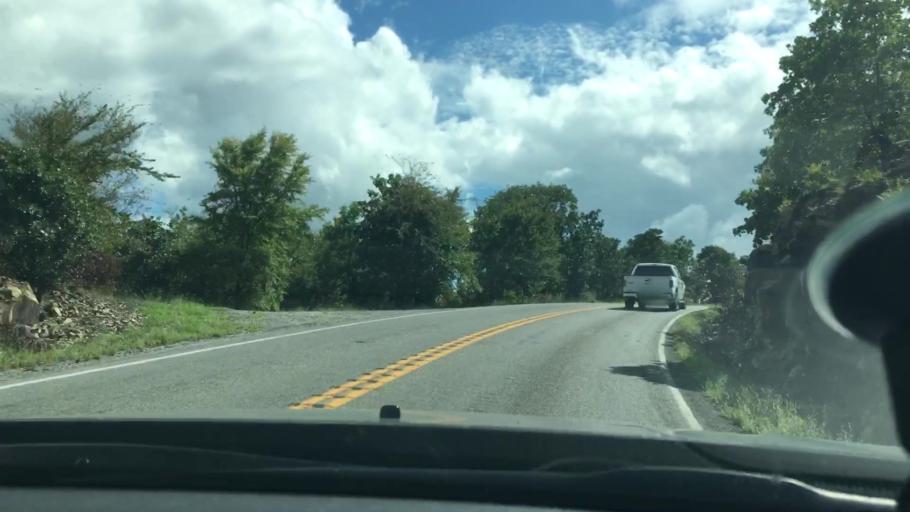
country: US
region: Oklahoma
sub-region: Sequoyah County
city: Vian
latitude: 35.6310
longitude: -94.9638
